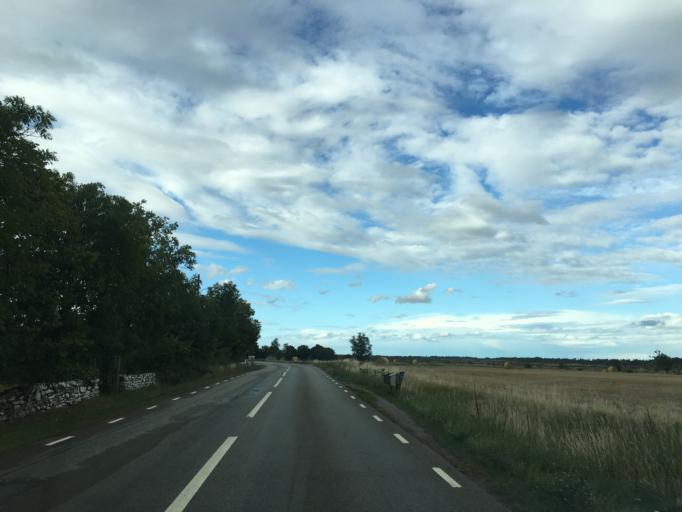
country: SE
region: Kalmar
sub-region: Morbylanga Kommun
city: Moerbylanga
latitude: 56.3891
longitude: 16.4358
